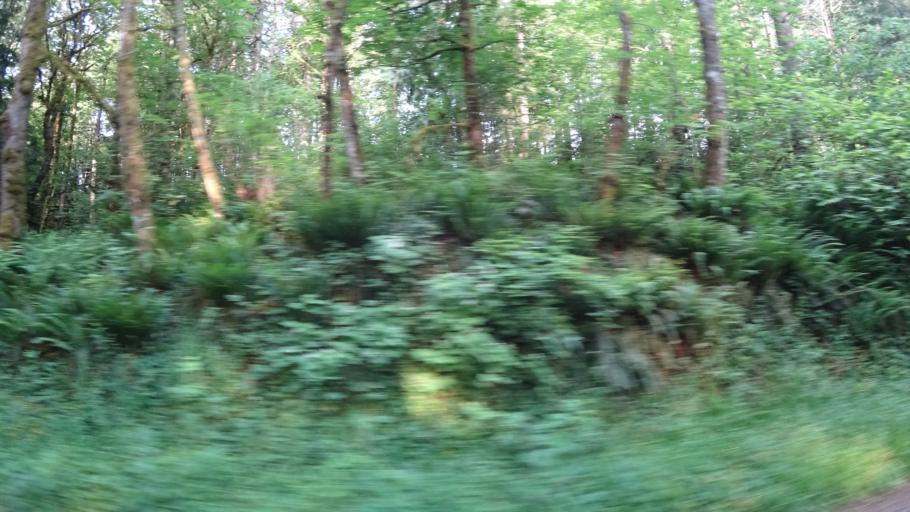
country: US
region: Oregon
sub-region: Clackamas County
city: Happy Valley
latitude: 45.4521
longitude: -122.5016
